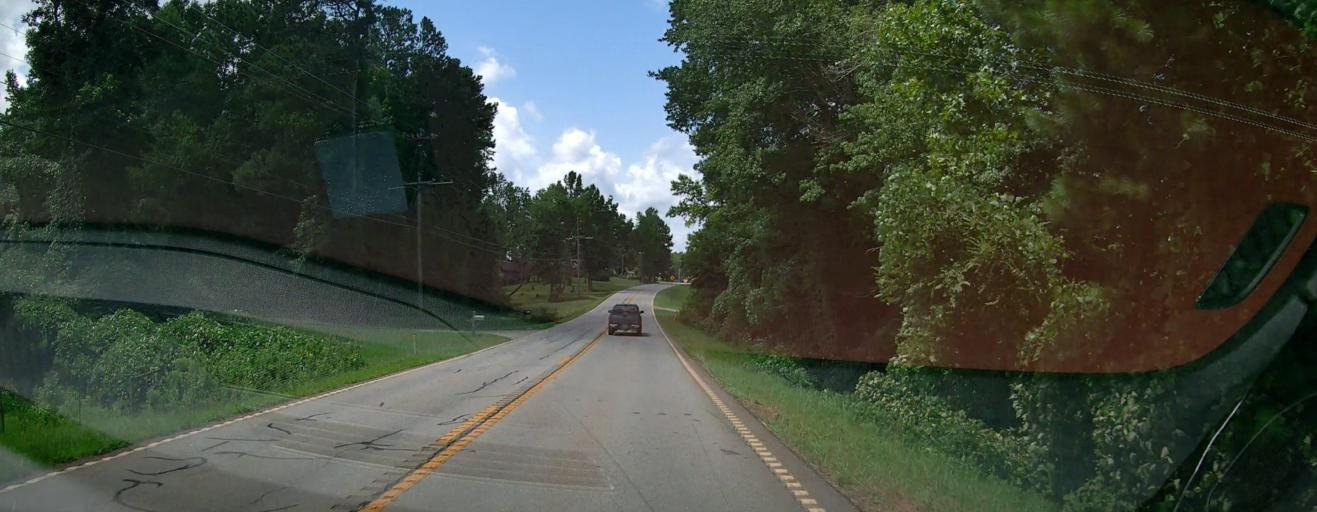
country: US
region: Georgia
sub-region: Carroll County
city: Bowdon
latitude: 33.3892
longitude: -85.2515
